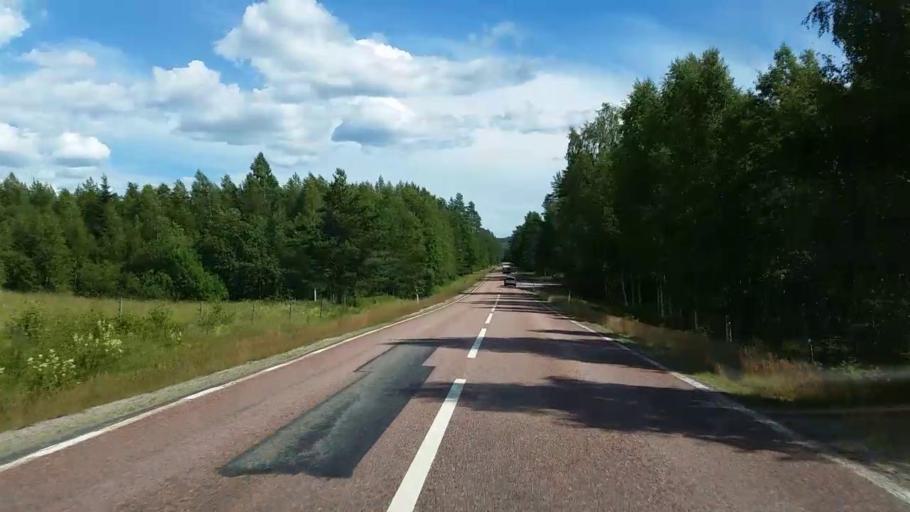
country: SE
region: Gaevleborg
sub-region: Ovanakers Kommun
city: Edsbyn
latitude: 61.3464
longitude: 15.6442
